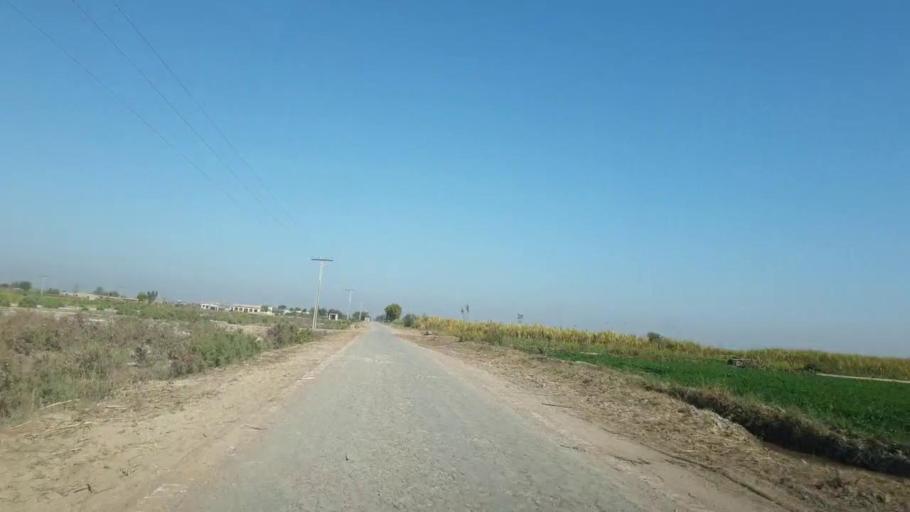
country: PK
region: Sindh
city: Mirpur Khas
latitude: 25.5934
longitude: 69.0453
